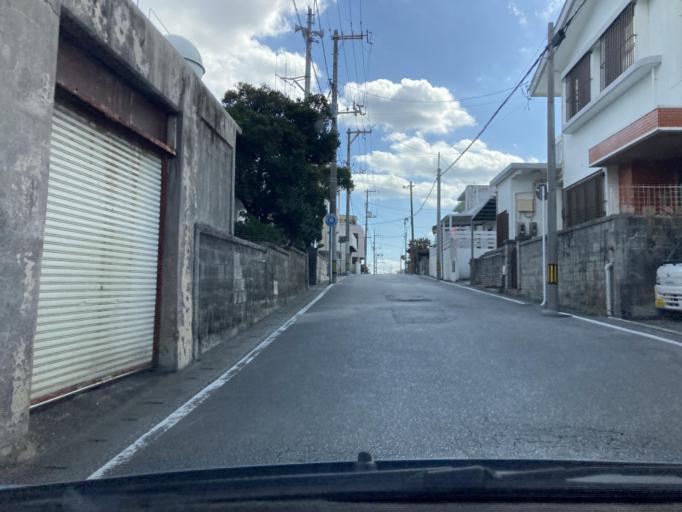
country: JP
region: Okinawa
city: Okinawa
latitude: 26.3413
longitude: 127.8064
